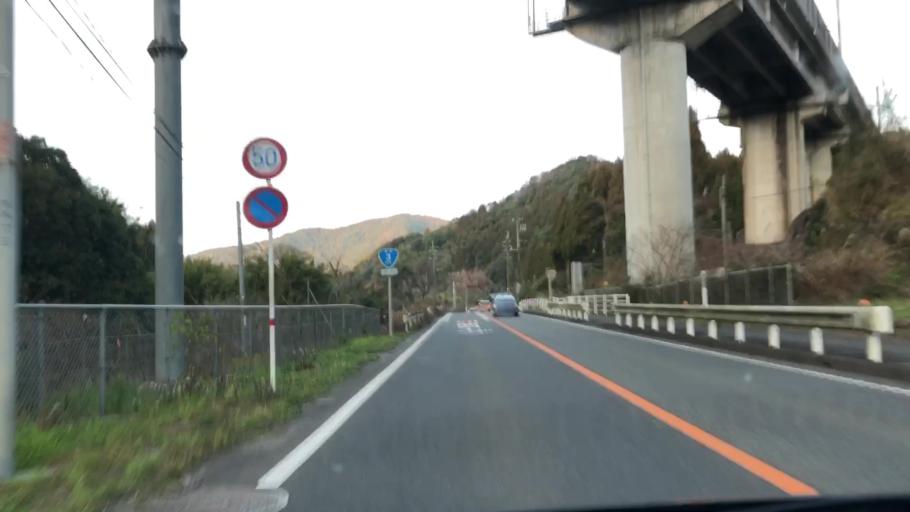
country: JP
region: Kumamoto
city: Minamata
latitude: 32.2178
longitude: 130.4377
